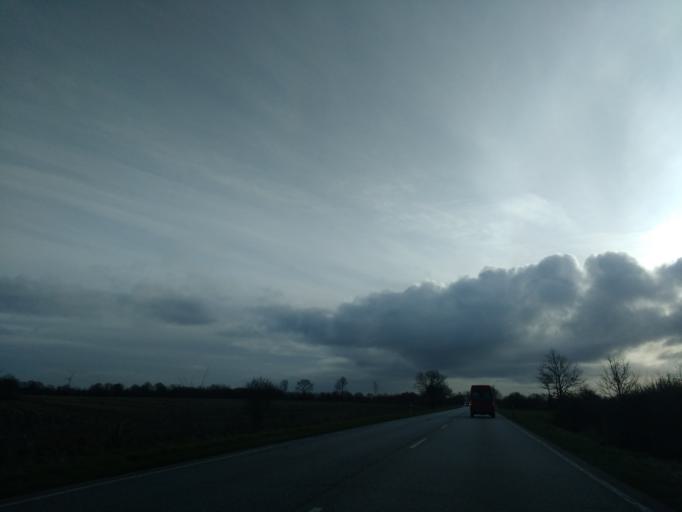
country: DE
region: Schleswig-Holstein
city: Krogaspe
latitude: 54.1320
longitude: 9.9142
